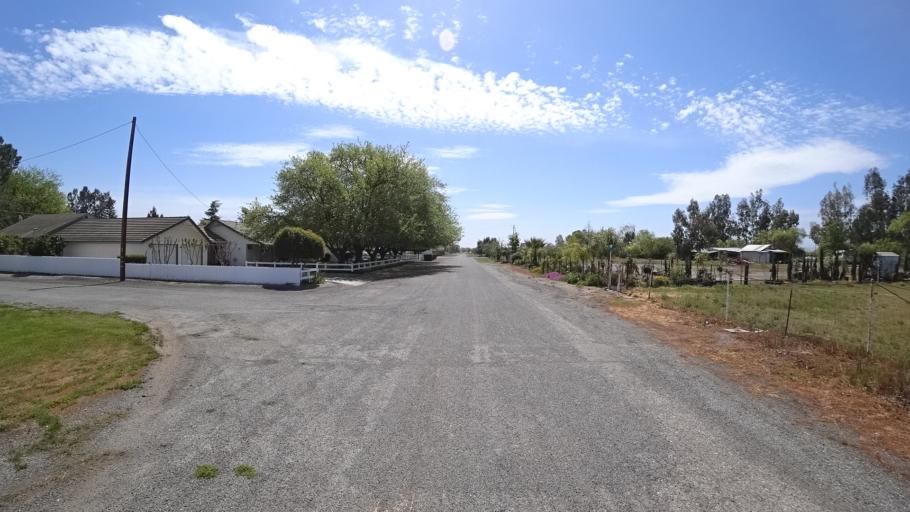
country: US
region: California
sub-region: Glenn County
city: Willows
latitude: 39.6196
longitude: -122.1966
